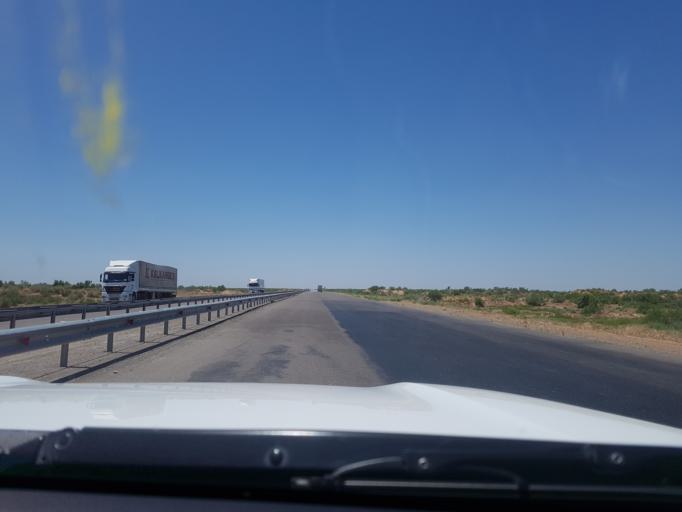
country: TM
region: Mary
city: Mary
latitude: 37.3056
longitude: 61.3753
